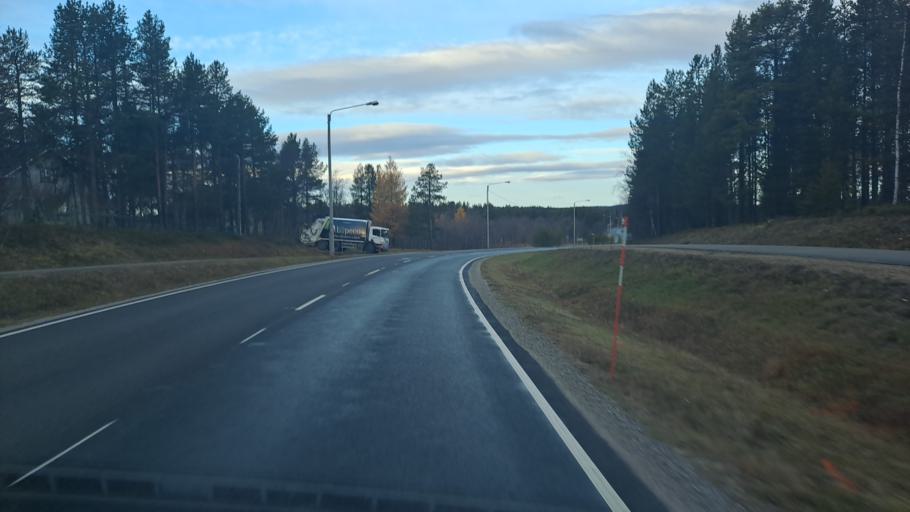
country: FI
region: Lapland
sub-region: Pohjois-Lappi
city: Inari
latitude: 68.9006
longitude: 27.0468
